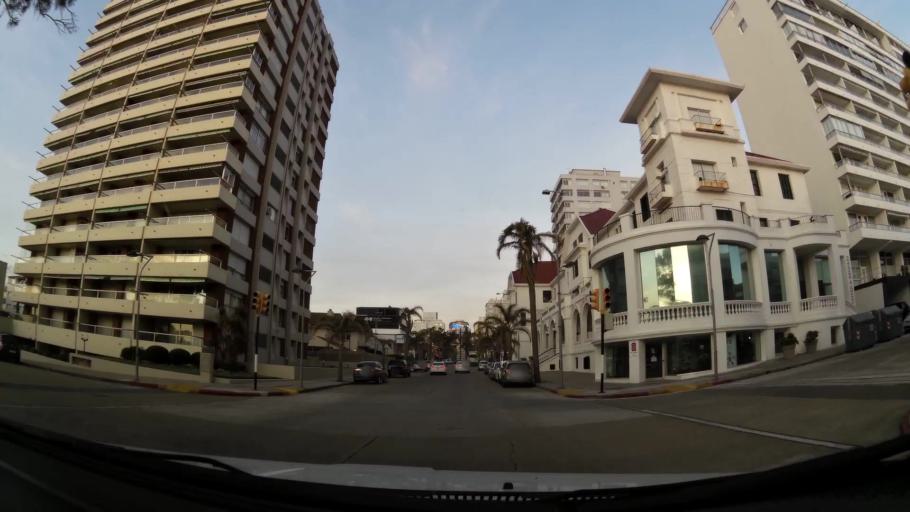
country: UY
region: Maldonado
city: Punta del Este
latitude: -34.9617
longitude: -54.9448
